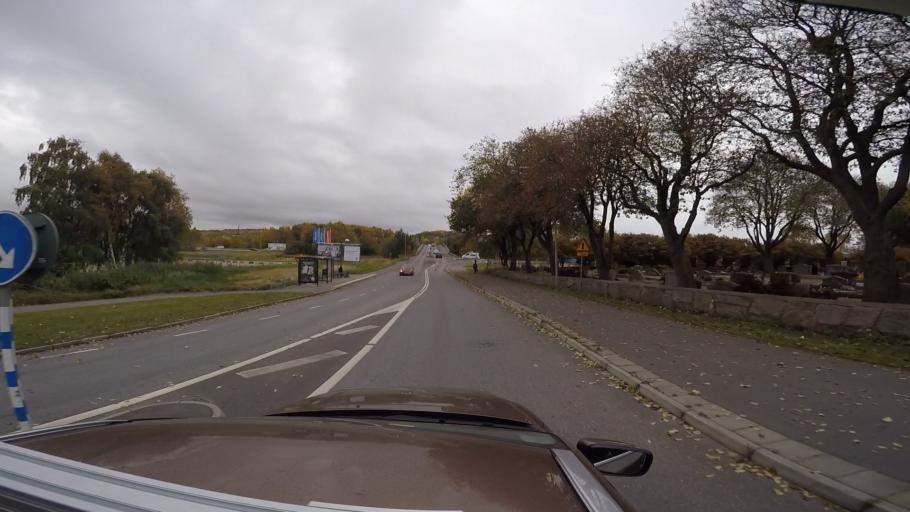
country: SE
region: Vaestra Goetaland
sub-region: Goteborg
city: Majorna
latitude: 57.6476
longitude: 11.9393
